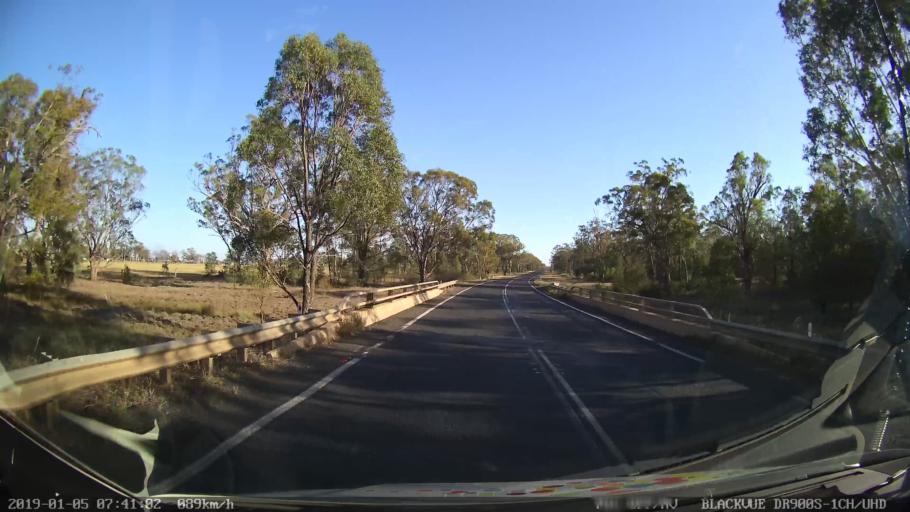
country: AU
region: New South Wales
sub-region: Gilgandra
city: Gilgandra
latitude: -31.9159
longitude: 148.6193
